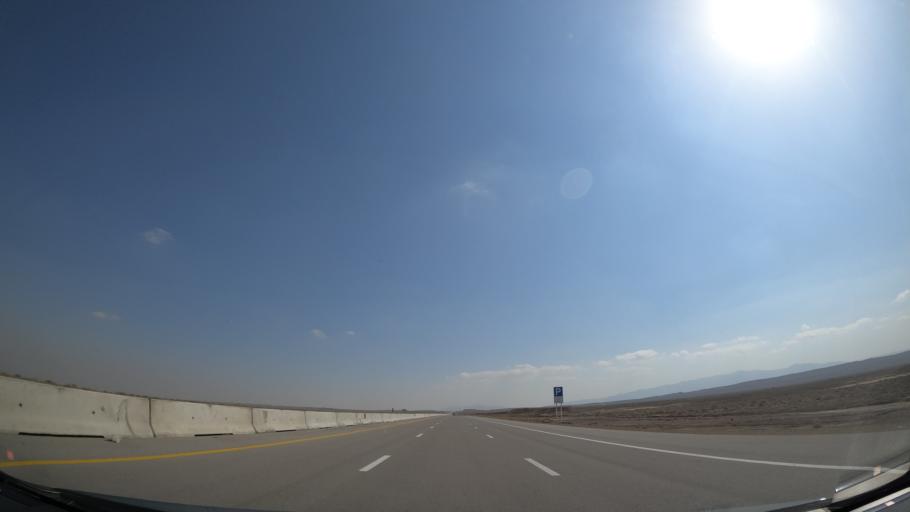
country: IR
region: Alborz
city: Nazarabad
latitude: 35.8212
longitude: 50.5132
